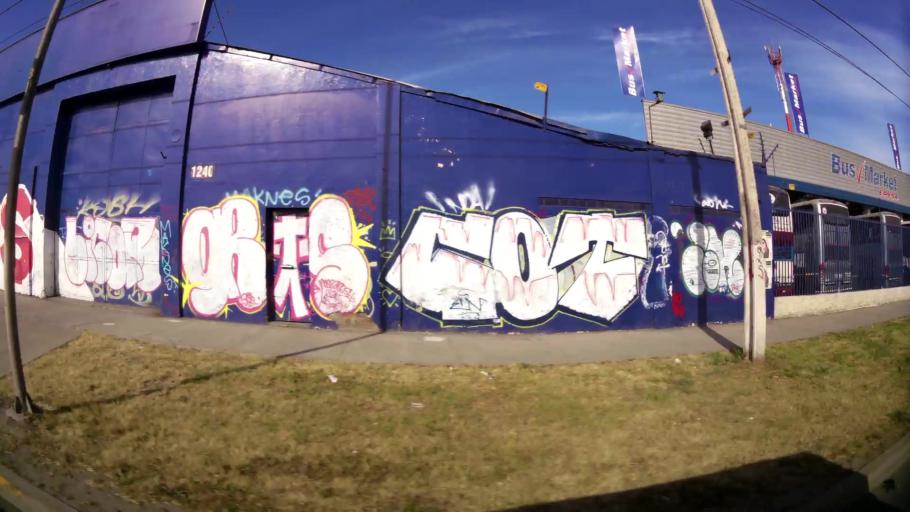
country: CL
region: Santiago Metropolitan
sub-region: Provincia de Santiago
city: Santiago
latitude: -33.4648
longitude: -70.6880
